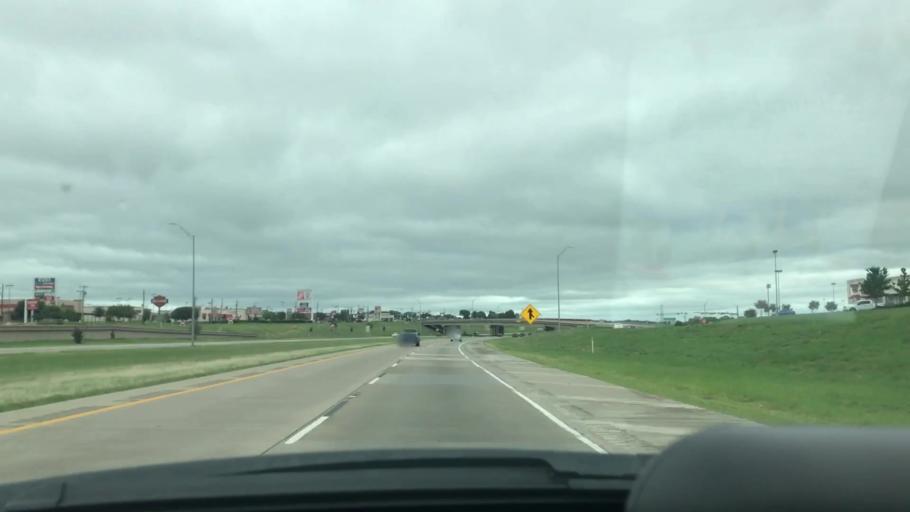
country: US
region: Texas
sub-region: Grayson County
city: Sherman
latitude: 33.6770
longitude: -96.6088
